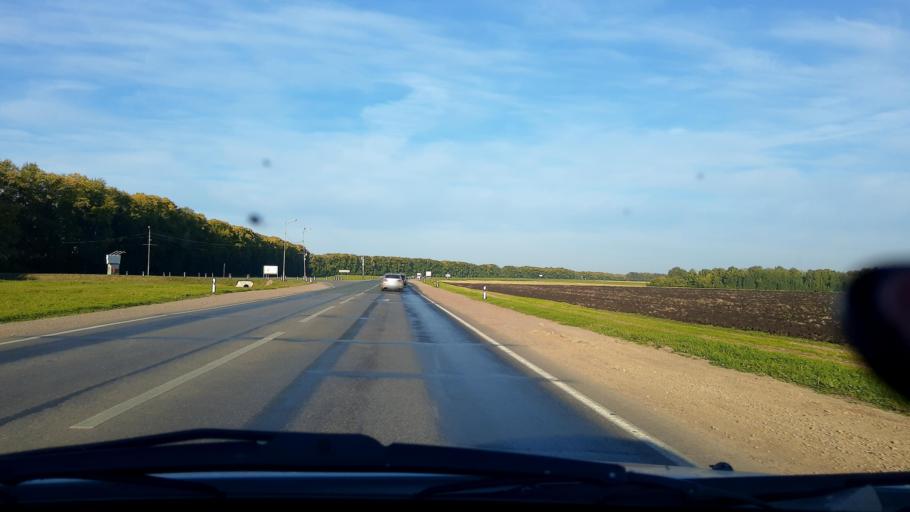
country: RU
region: Bashkortostan
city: Karmaskaly
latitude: 54.3853
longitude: 56.1544
